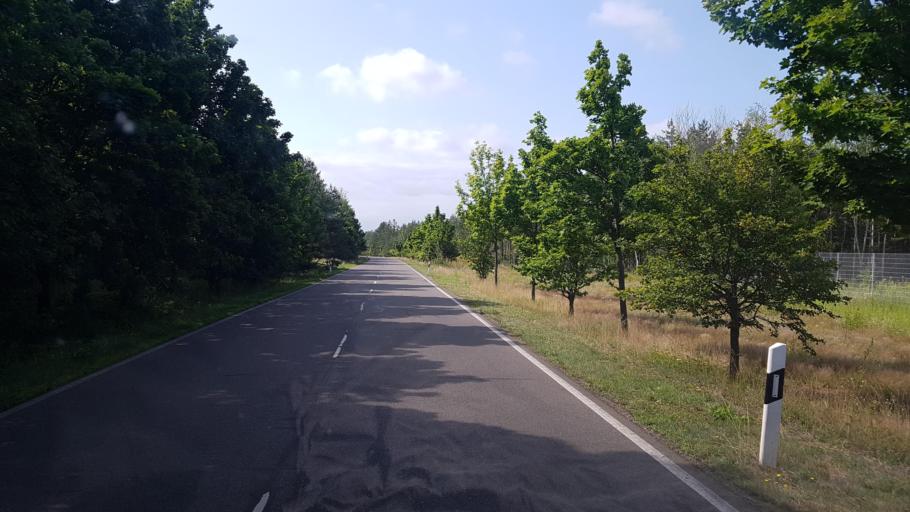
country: DE
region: Brandenburg
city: Grossraschen
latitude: 51.5924
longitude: 14.0285
